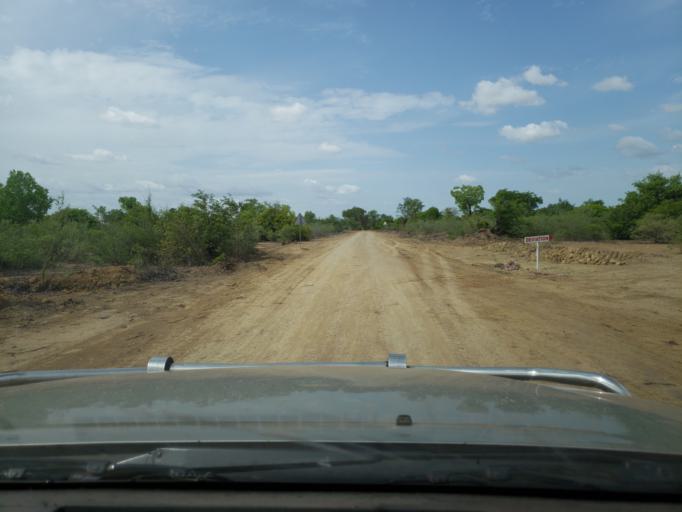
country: ML
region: Segou
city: Bla
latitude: 12.7638
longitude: -5.6225
